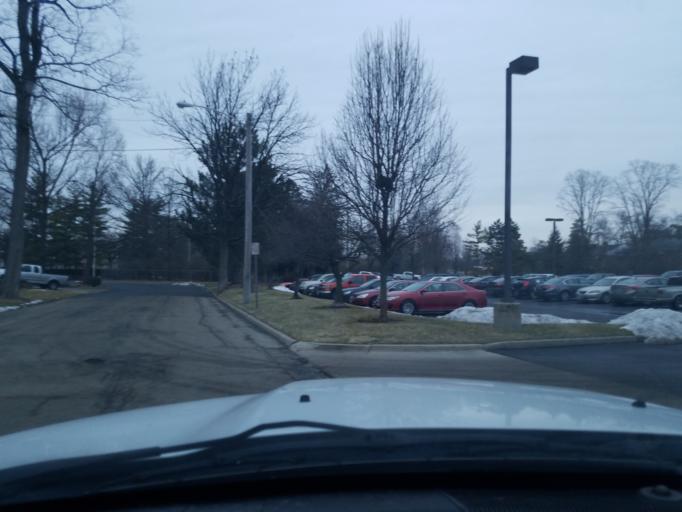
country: US
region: Ohio
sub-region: Montgomery County
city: Oakwood
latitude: 39.7178
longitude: -84.1604
